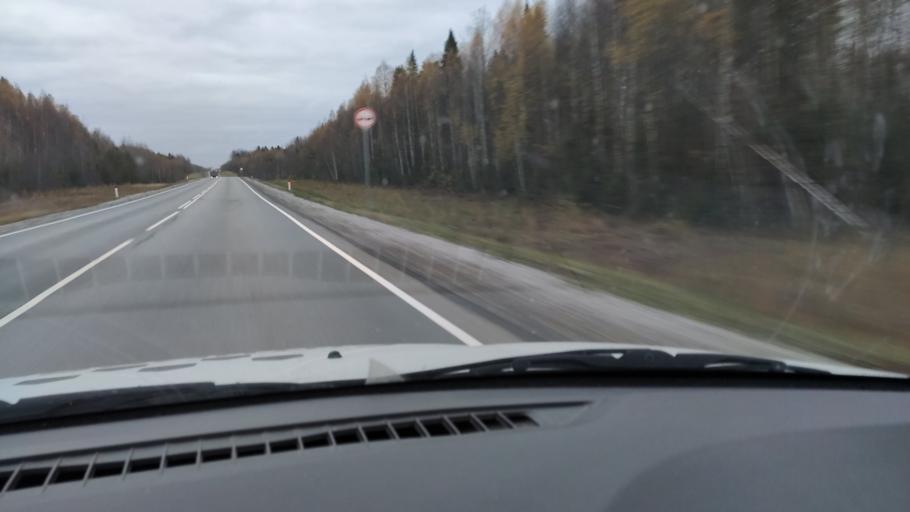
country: RU
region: Kirov
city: Lesnyye Polyany
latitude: 58.8336
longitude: 52.6625
